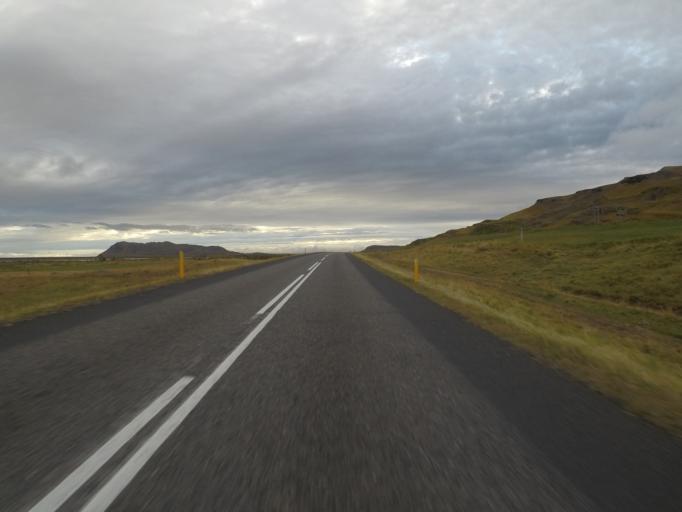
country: IS
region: South
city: Vestmannaeyjar
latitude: 64.0689
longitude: -20.0502
